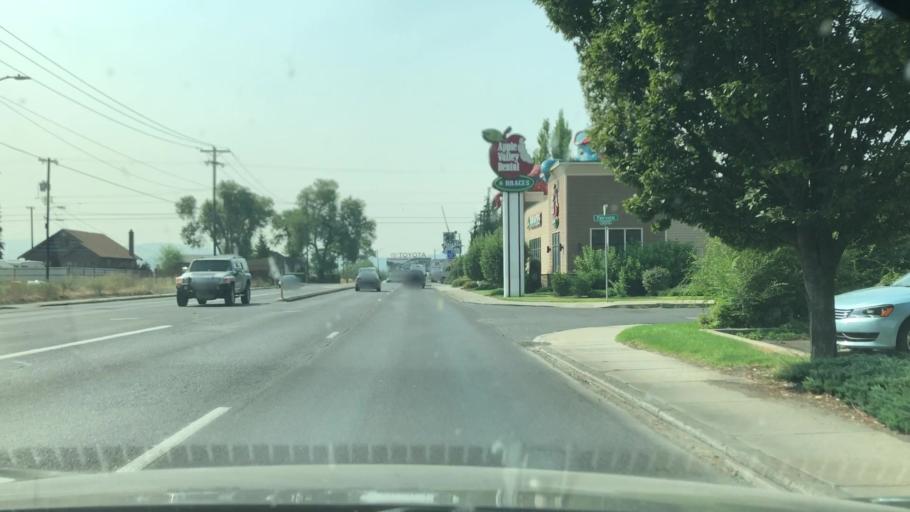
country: US
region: Washington
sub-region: Spokane County
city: Spokane
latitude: 47.6853
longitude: -117.3652
